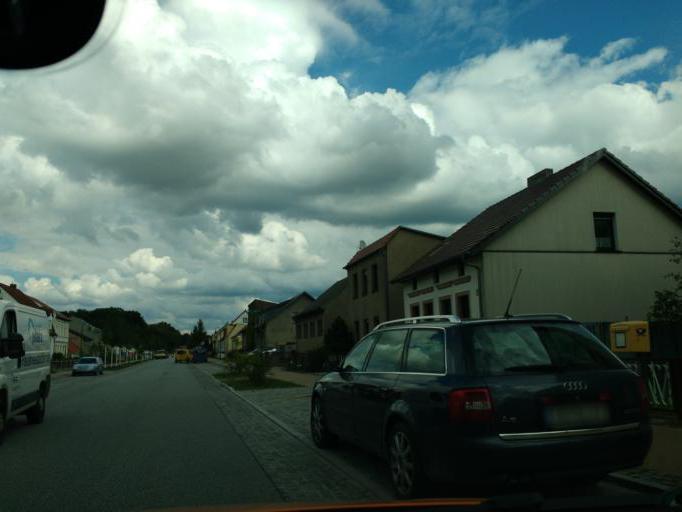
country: DE
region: Brandenburg
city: Marienwerder
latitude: 52.8535
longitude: 13.5291
